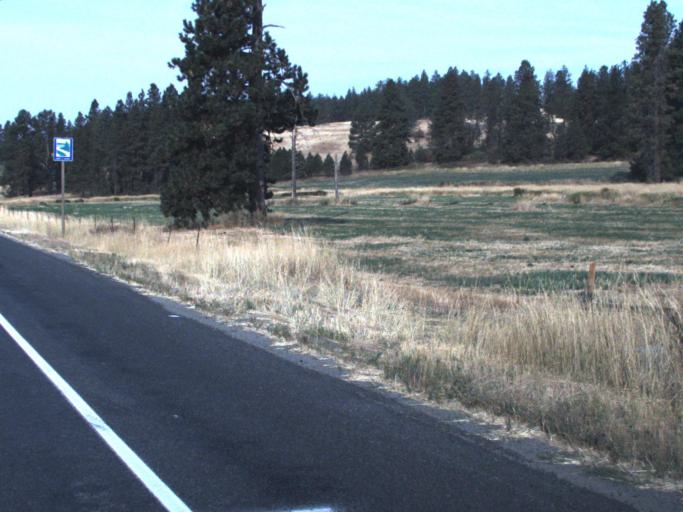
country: US
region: Idaho
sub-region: Benewah County
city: Plummer
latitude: 47.4389
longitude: -117.0887
